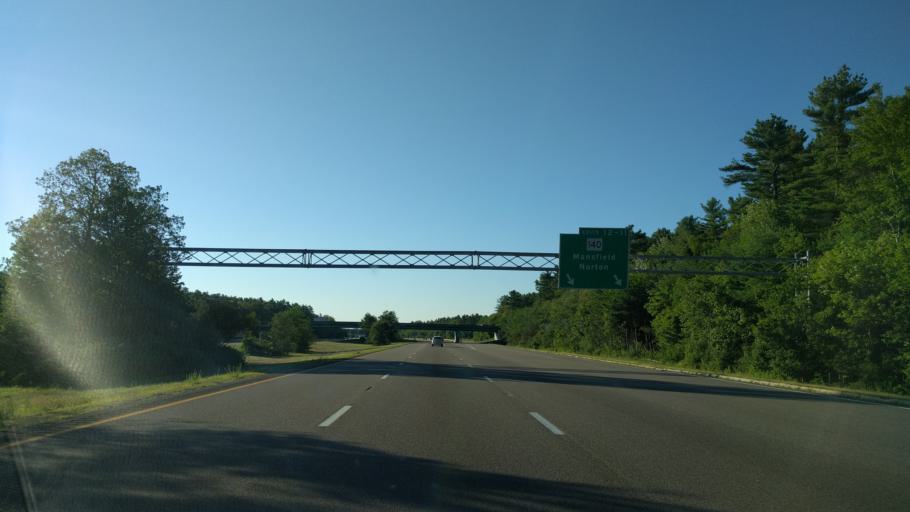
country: US
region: Massachusetts
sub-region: Bristol County
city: Mansfield Center
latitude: 42.0083
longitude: -71.2273
